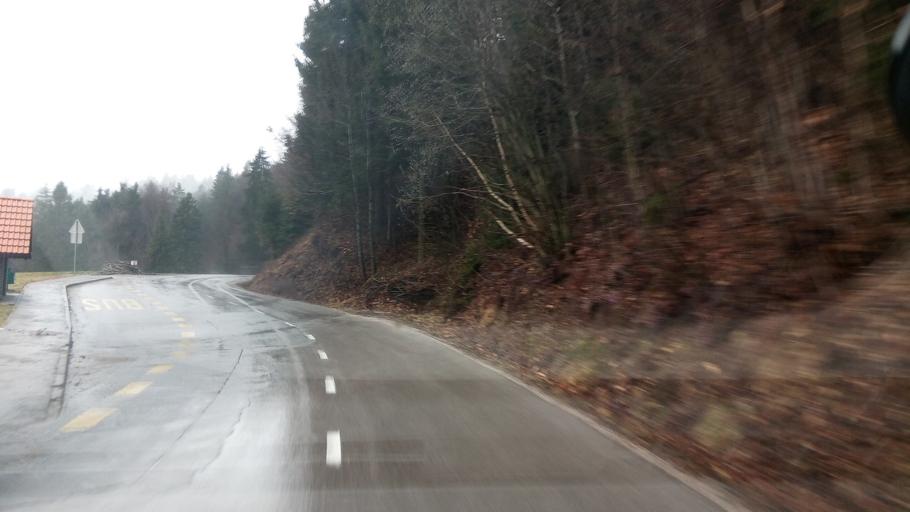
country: SI
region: Ziri
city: Ziri
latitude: 46.0200
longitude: 14.1950
